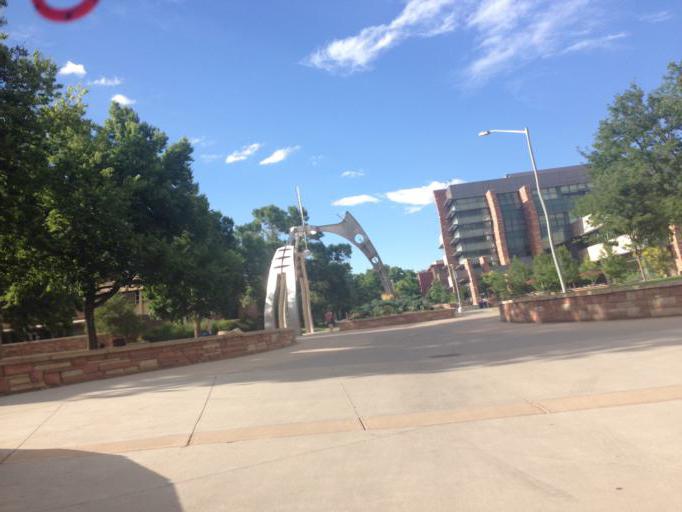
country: US
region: Colorado
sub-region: Larimer County
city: Fort Collins
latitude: 40.5703
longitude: -105.0837
